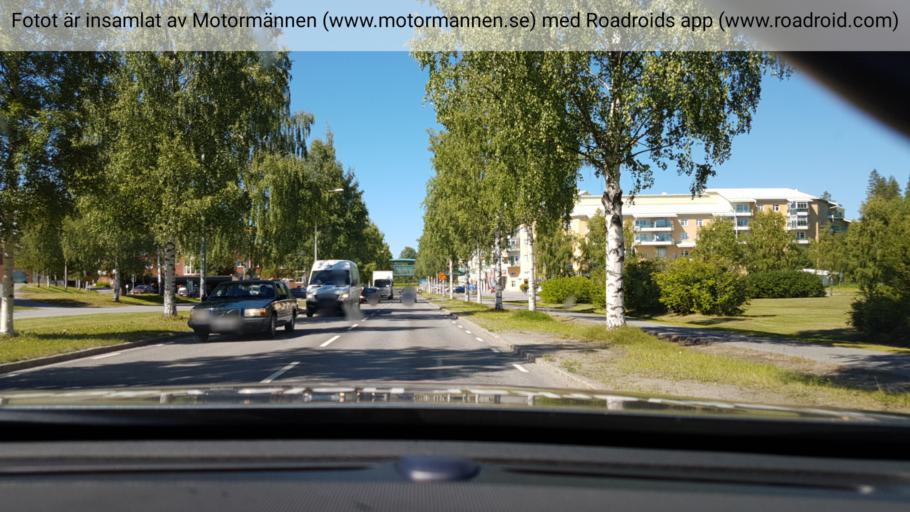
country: SE
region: Vaesterbotten
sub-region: Skelleftea Kommun
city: Skelleftea
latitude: 64.7592
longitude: 20.9565
